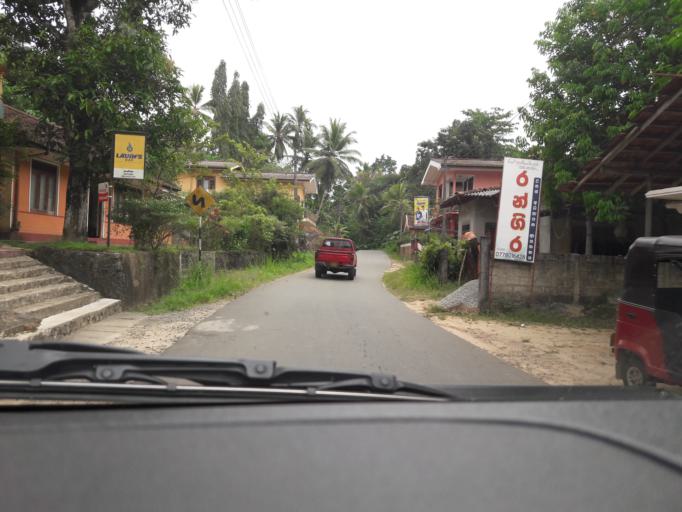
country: LK
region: Southern
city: Galle
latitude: 6.1827
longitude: 80.2982
